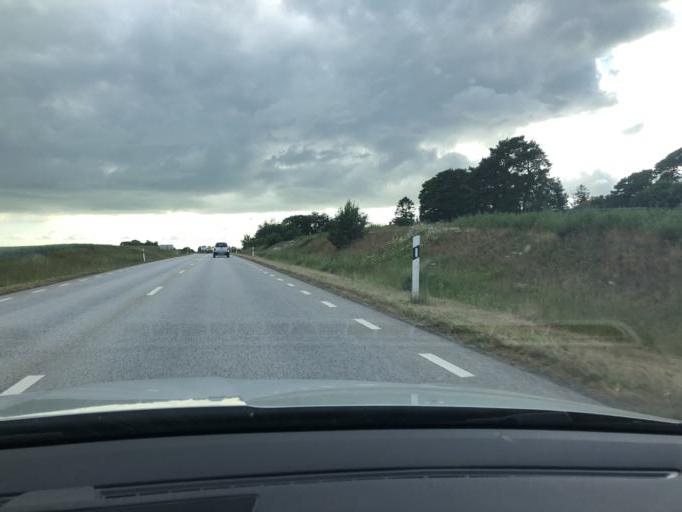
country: SE
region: Skane
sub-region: Simrishamns Kommun
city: Simrishamn
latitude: 55.5355
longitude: 14.2836
